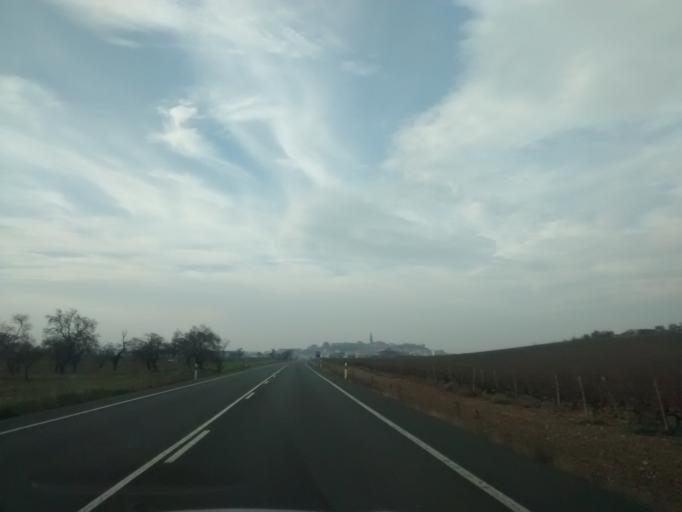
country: ES
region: La Rioja
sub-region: Provincia de La Rioja
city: Briones
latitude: 42.5325
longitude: -2.7652
